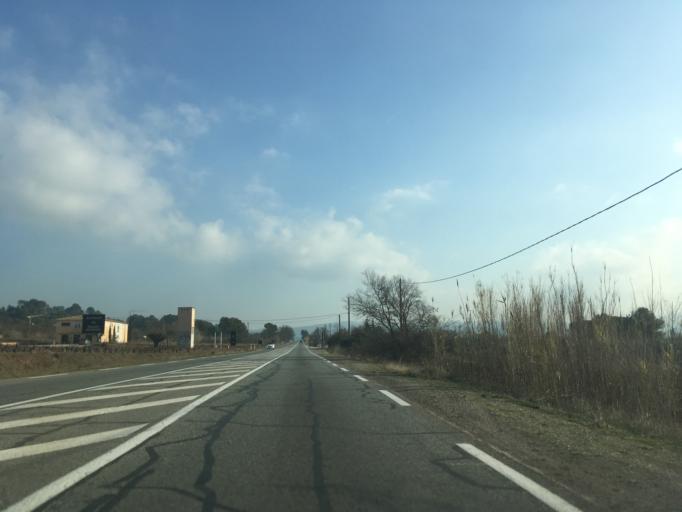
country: FR
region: Provence-Alpes-Cote d'Azur
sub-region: Departement du Var
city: Vidauban
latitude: 43.4041
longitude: 6.3972
